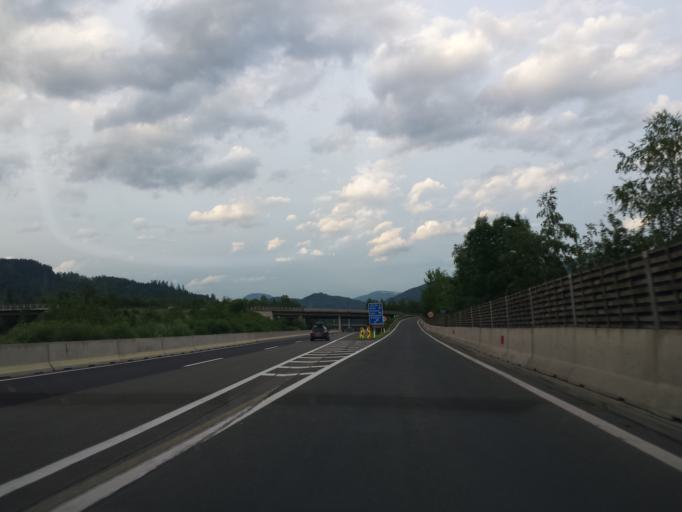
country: AT
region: Styria
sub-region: Politischer Bezirk Leoben
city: Sankt Michael in Obersteiermark
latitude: 47.3366
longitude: 15.0037
